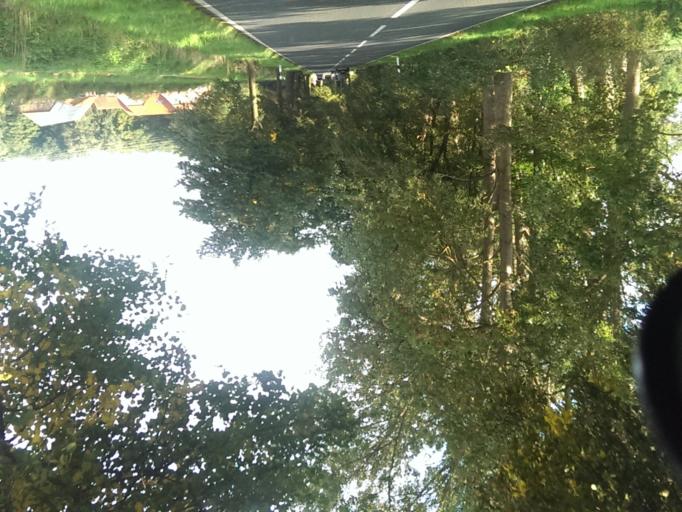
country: DE
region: Lower Saxony
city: Wunstorf
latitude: 52.4541
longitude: 9.4658
